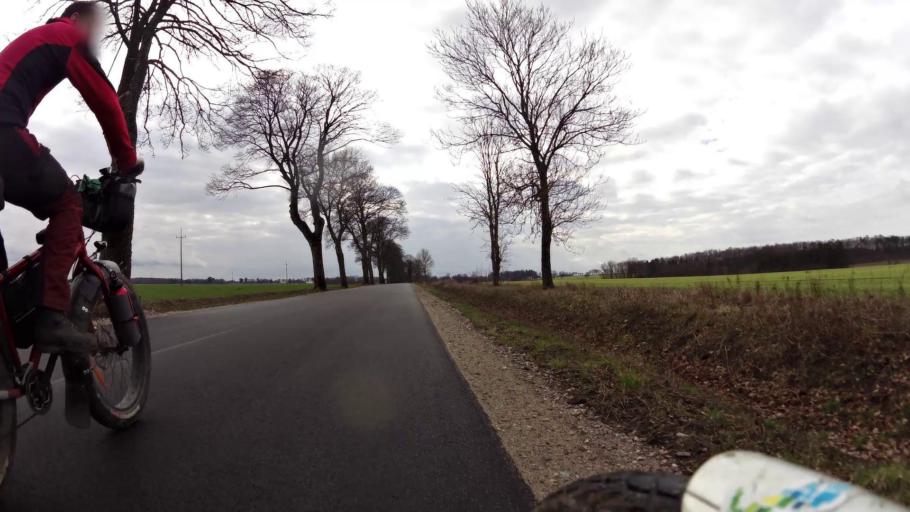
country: PL
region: Pomeranian Voivodeship
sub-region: Powiat bytowski
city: Kolczyglowy
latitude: 54.2339
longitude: 17.2424
